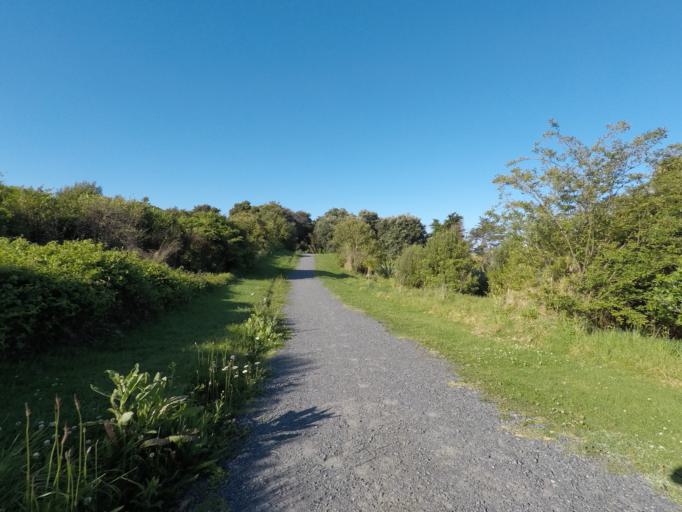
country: NZ
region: Auckland
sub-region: Auckland
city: Rosebank
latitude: -36.8412
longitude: 174.6594
